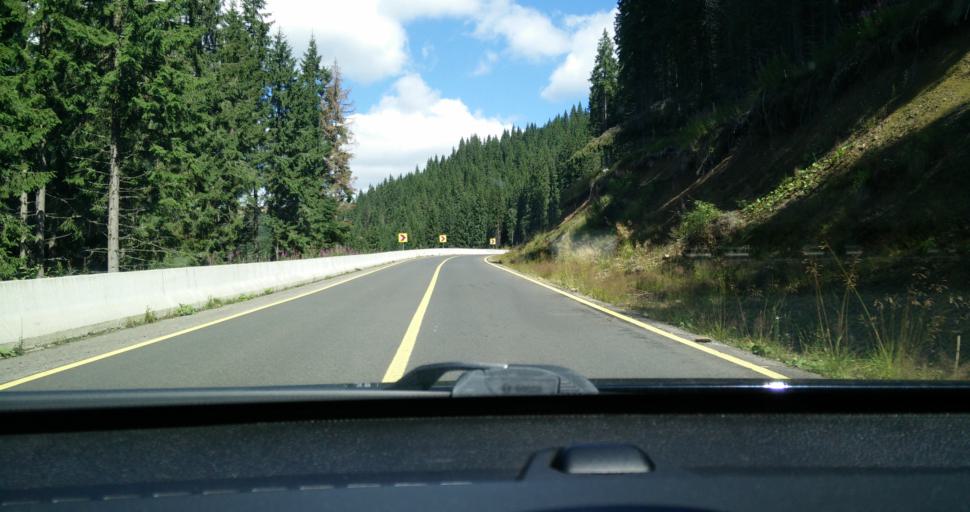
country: RO
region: Hunedoara
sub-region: Oras Petrila
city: Petrila
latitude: 45.4522
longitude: 23.6171
